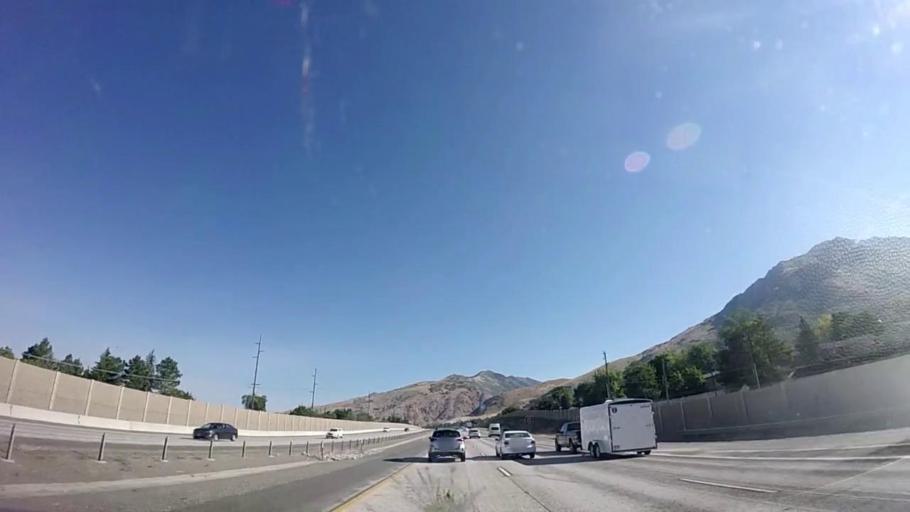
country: US
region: Utah
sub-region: Salt Lake County
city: Mount Olympus
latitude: 40.6931
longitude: -111.7965
